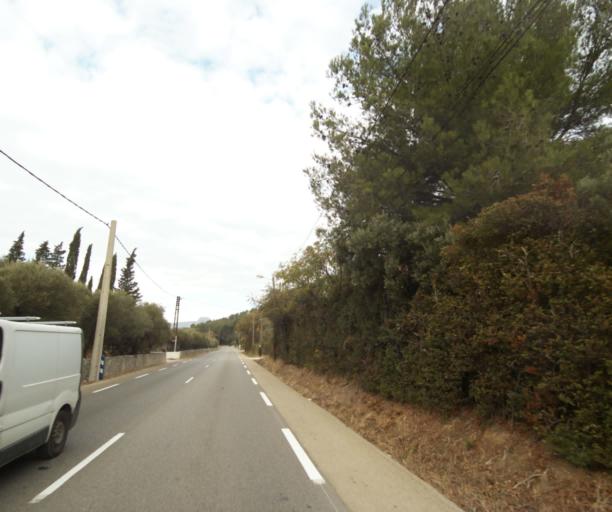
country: FR
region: Provence-Alpes-Cote d'Azur
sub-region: Departement des Bouches-du-Rhone
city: Gemenos
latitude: 43.2775
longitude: 5.6332
